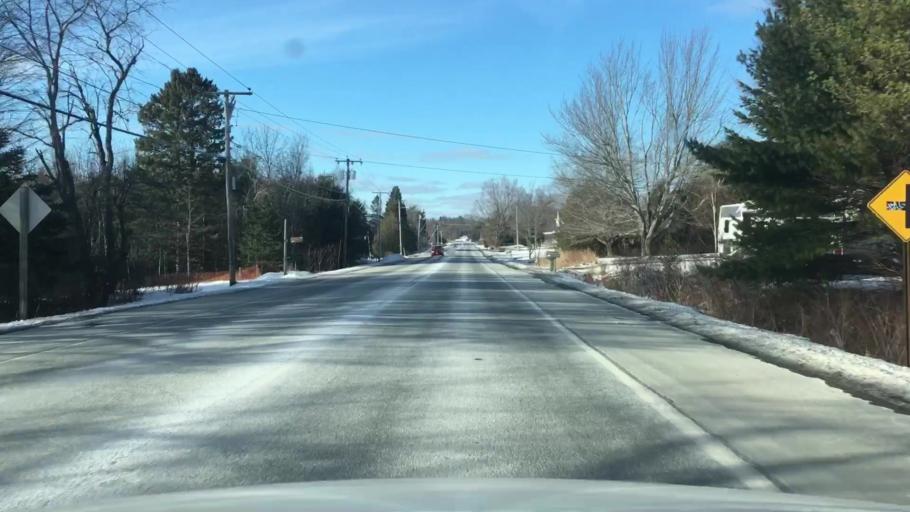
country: US
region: Maine
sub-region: Penobscot County
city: Holden
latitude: 44.7972
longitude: -68.5929
